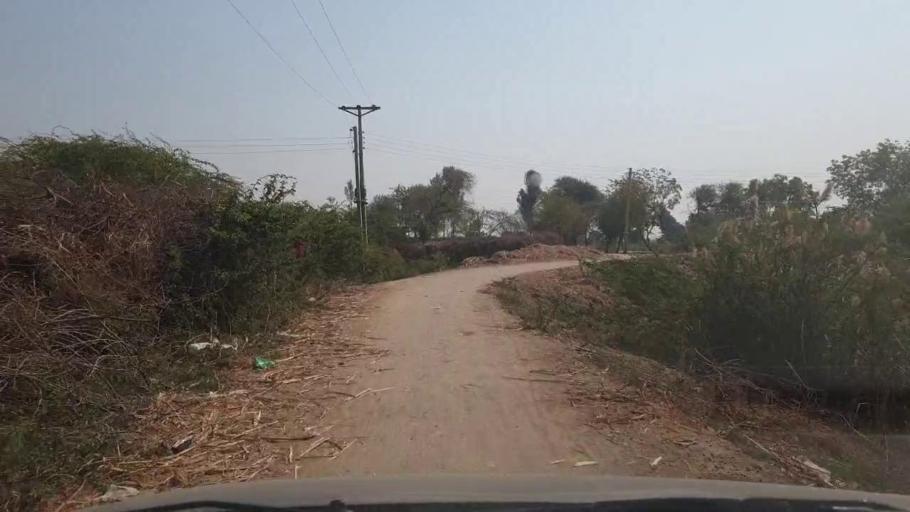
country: PK
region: Sindh
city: Mirwah Gorchani
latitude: 25.2803
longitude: 69.1488
